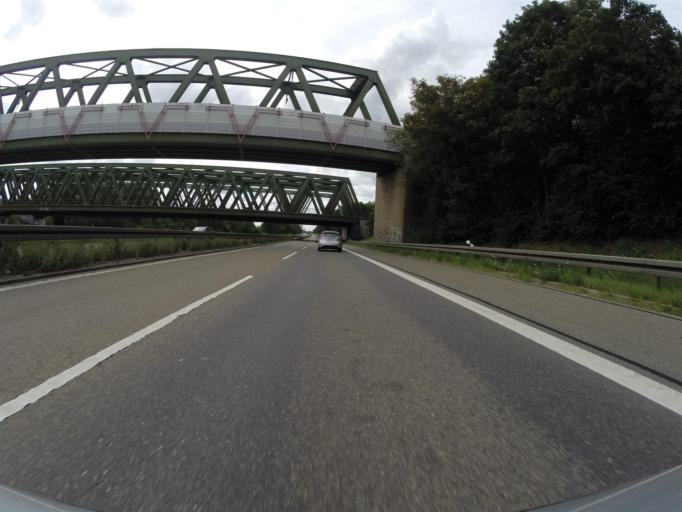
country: DE
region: Bavaria
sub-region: Regierungsbezirk Mittelfranken
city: Grossreuth bei Schweinau
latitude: 49.4187
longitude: 11.0520
